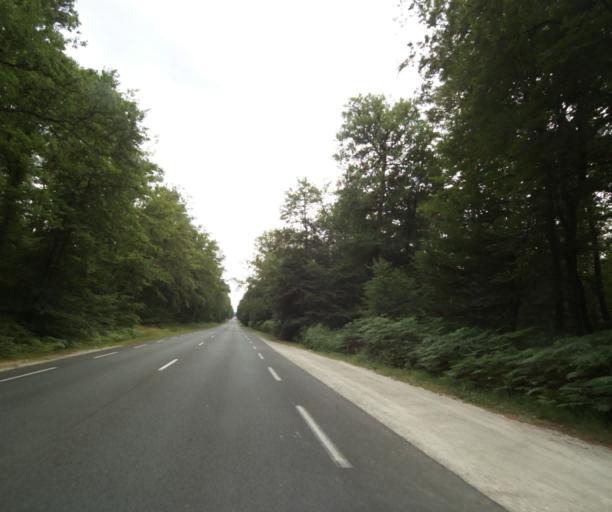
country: FR
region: Ile-de-France
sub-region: Departement de Seine-et-Marne
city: Bois-le-Roi
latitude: 48.4688
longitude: 2.6804
